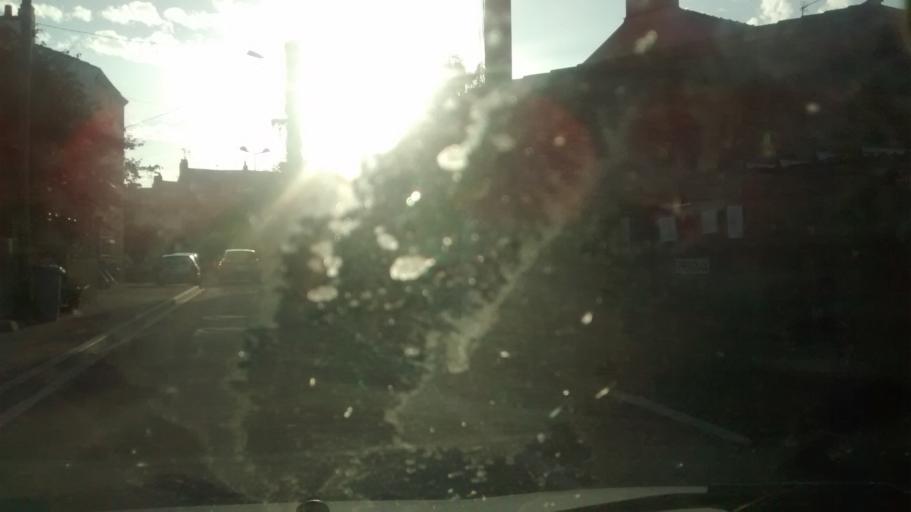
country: FR
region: Pays de la Loire
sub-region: Departement de la Loire-Atlantique
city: Reze
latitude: 47.1947
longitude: -1.5799
